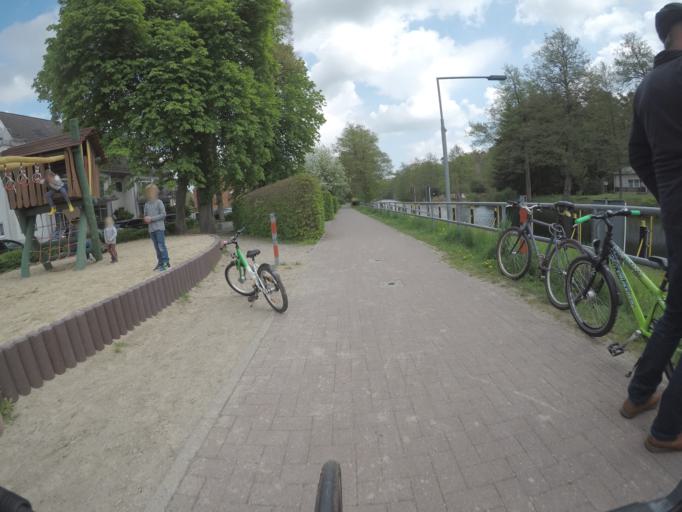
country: DE
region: Brandenburg
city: Marienwerder
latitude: 52.8926
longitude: 13.6391
